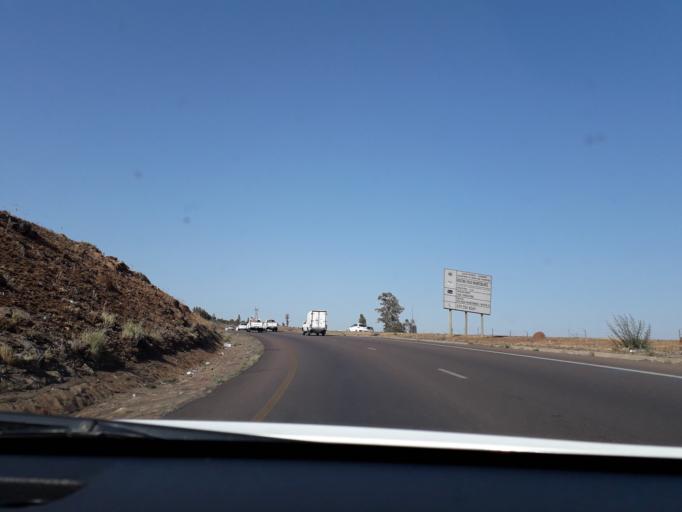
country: ZA
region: Gauteng
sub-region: City of Tshwane Metropolitan Municipality
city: Pretoria
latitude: -25.7861
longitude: 28.1910
